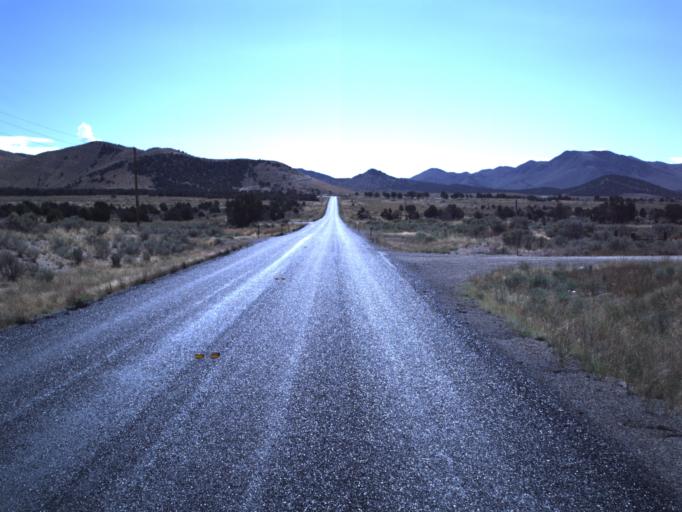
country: US
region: Utah
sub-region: Juab County
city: Mona
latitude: 39.9259
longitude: -112.1580
